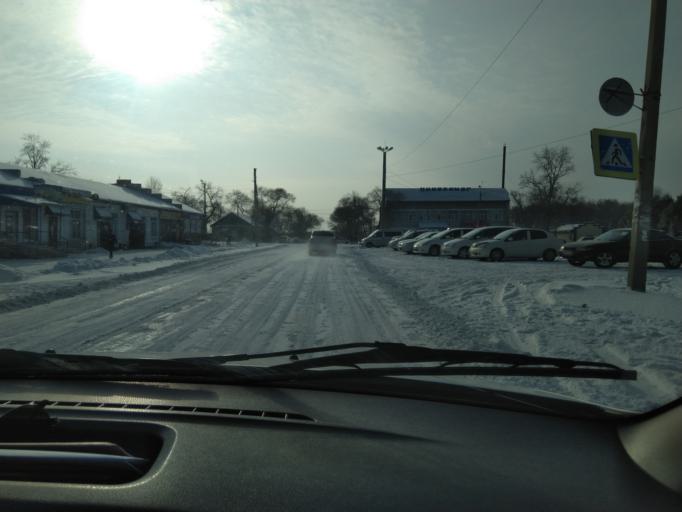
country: RU
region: Amur
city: Poyarkovo
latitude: 49.6216
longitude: 128.6511
